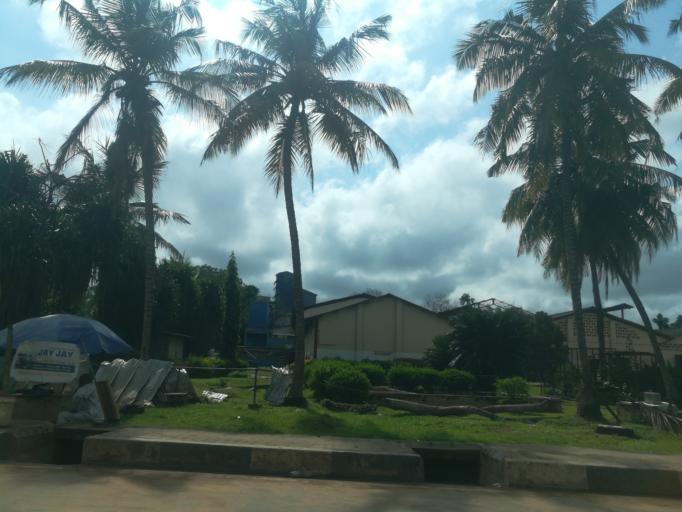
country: NG
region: Oyo
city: Ibadan
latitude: 7.3443
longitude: 3.8755
